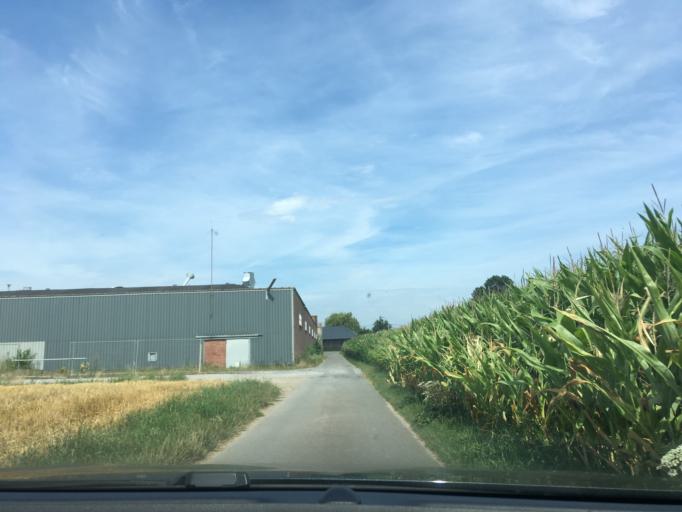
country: BE
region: Flanders
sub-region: Provincie West-Vlaanderen
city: Moorslede
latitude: 50.9001
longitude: 3.1021
